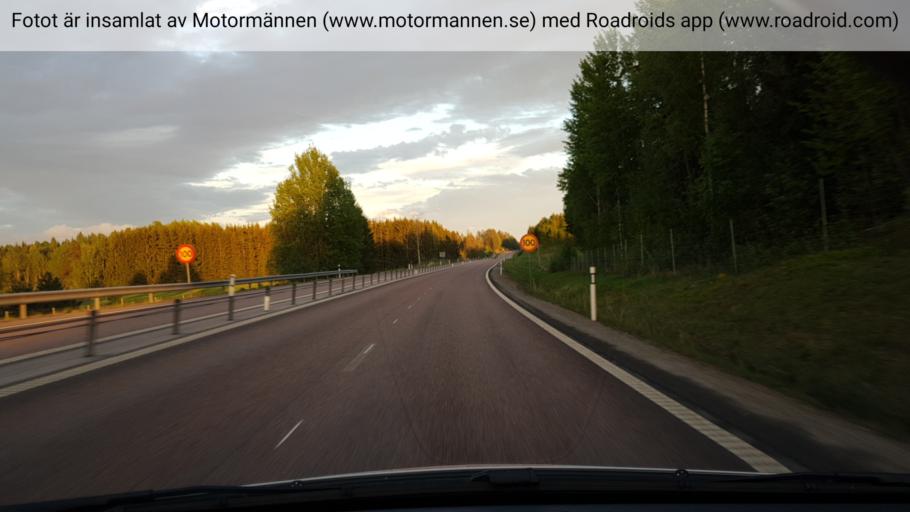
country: SE
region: Vaestmanland
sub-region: Fagersta Kommun
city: Fagersta
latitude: 59.9768
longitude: 15.8253
